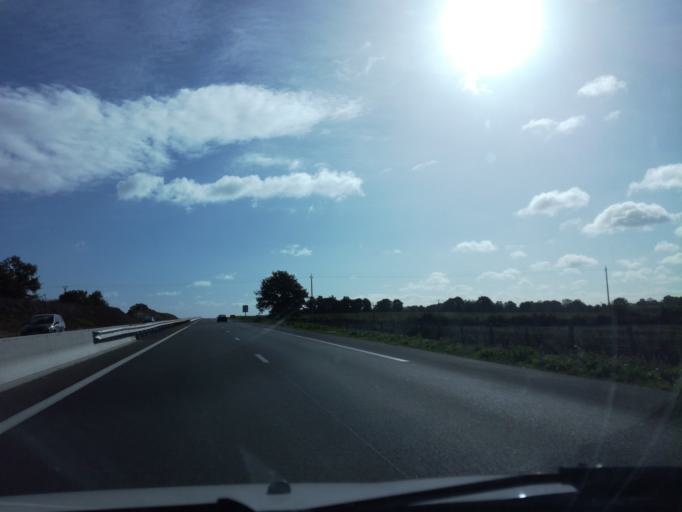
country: FR
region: Pays de la Loire
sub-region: Departement de Maine-et-Loire
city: Grez-Neuville
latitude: 47.5935
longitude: -0.7024
